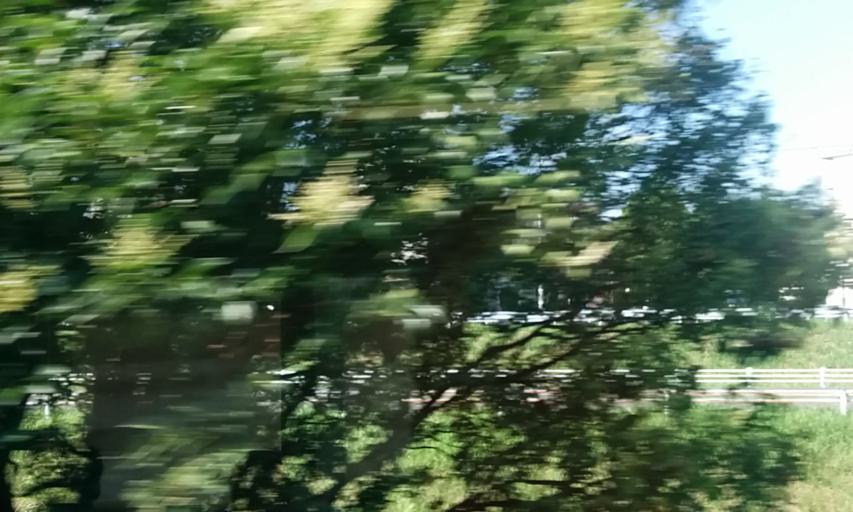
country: JP
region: Saitama
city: Kukichuo
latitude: 36.0914
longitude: 139.6625
